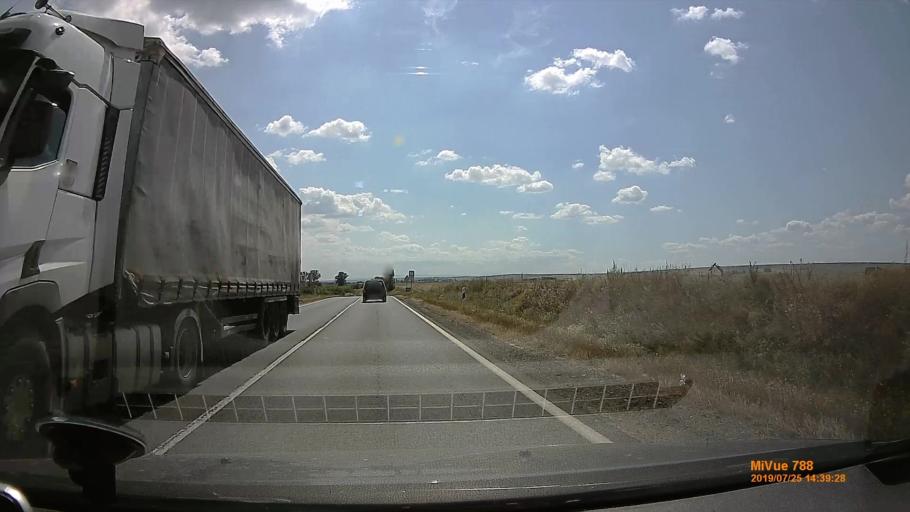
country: HU
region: Borsod-Abauj-Zemplen
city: Halmaj
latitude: 48.2992
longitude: 21.0529
